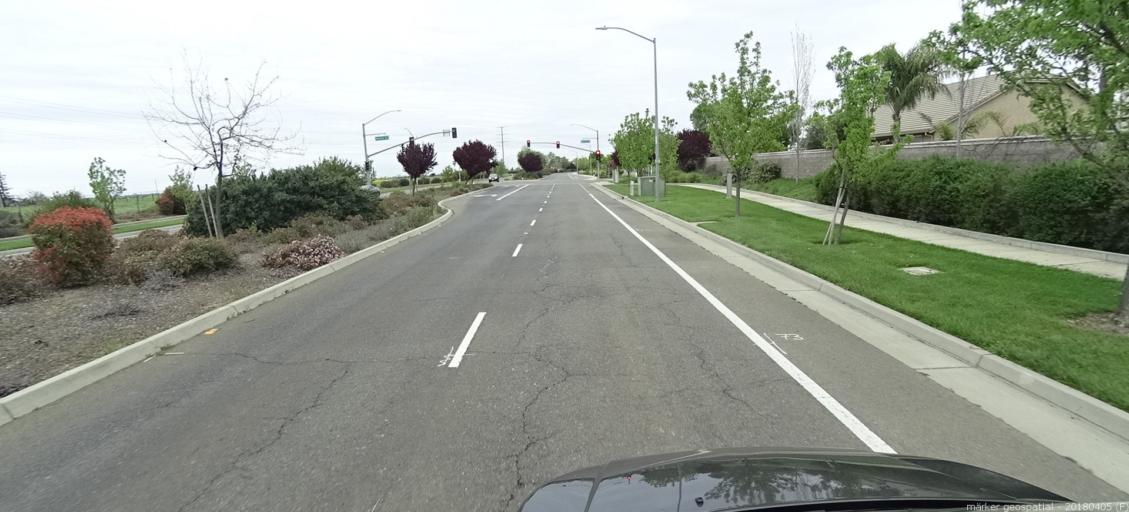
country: US
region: California
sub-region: Sacramento County
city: Laguna
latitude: 38.3814
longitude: -121.4484
